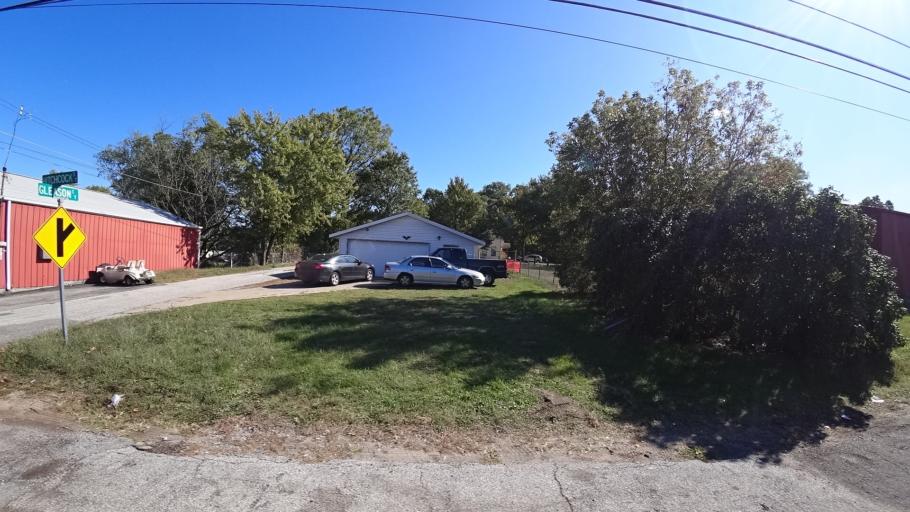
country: US
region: Indiana
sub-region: LaPorte County
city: Michigan City
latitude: 41.7020
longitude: -86.9140
